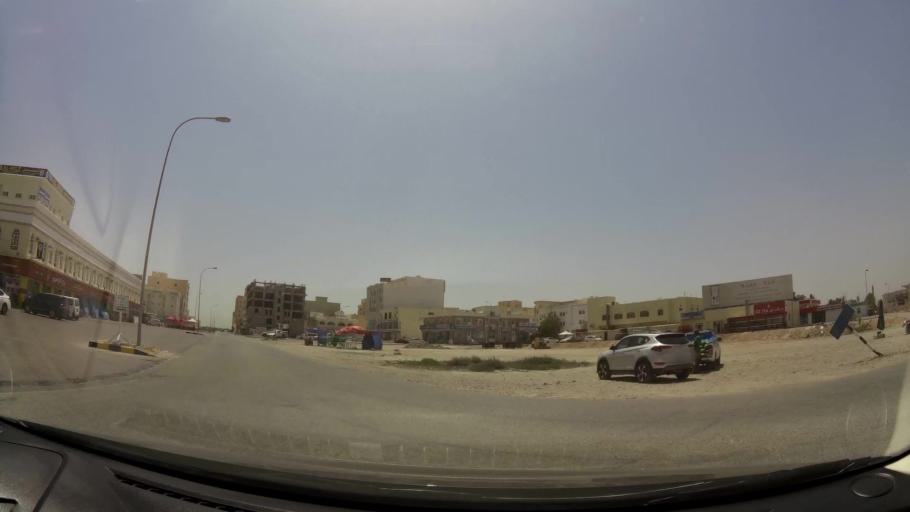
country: OM
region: Zufar
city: Salalah
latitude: 17.0520
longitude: 54.1532
